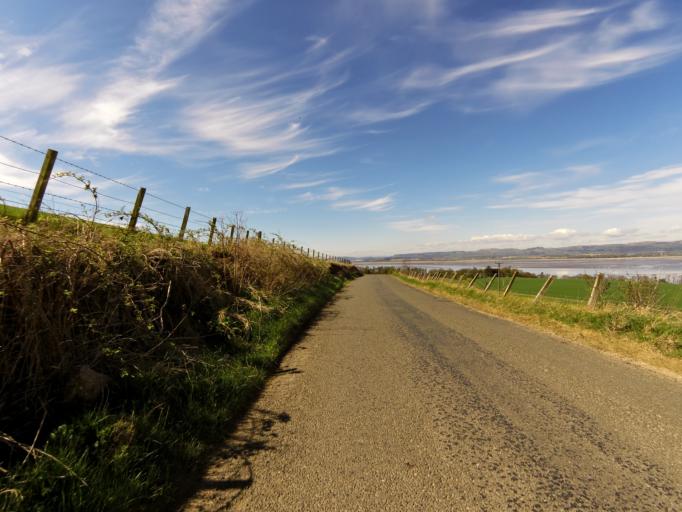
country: GB
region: Scotland
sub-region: Perth and Kinross
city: Errol
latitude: 56.3882
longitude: -3.1019
